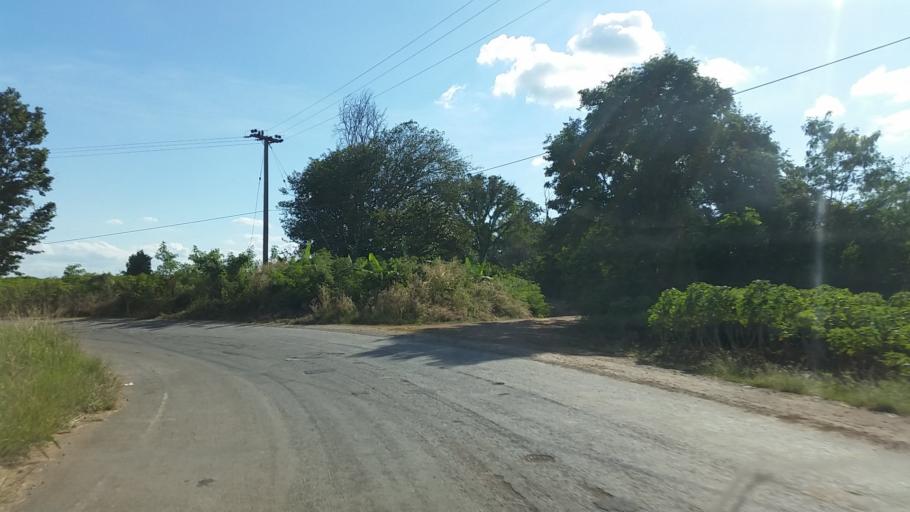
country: TH
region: Chaiyaphum
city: Thep Sathit
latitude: 15.5486
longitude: 101.4491
